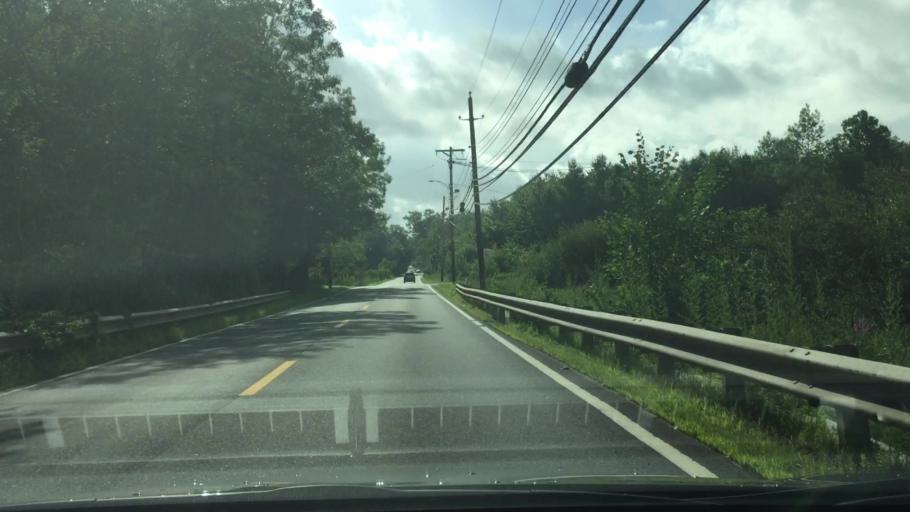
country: US
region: Massachusetts
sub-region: Middlesex County
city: Stow
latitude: 42.4787
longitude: -71.4908
